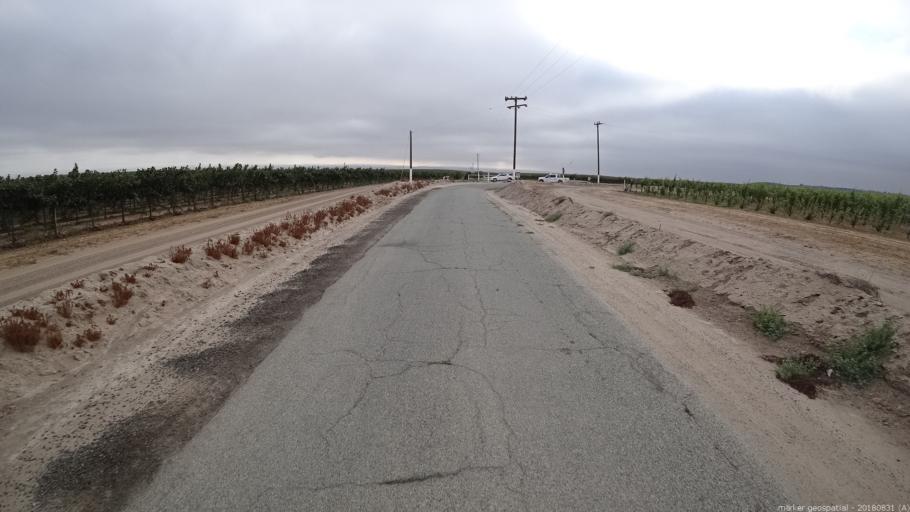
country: US
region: California
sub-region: Monterey County
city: King City
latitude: 36.1400
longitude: -121.0929
